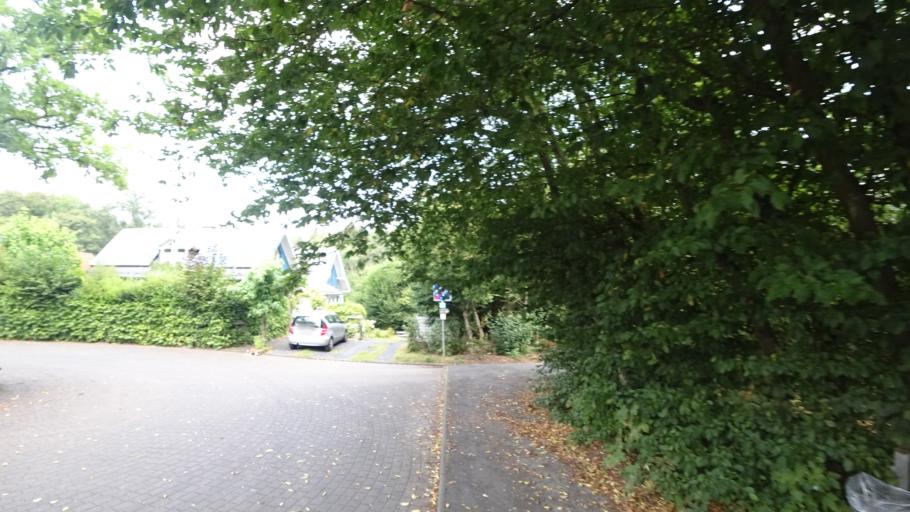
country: DE
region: Rheinland-Pfalz
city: Hohr-Grenzhausen
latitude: 50.4336
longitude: 7.6836
